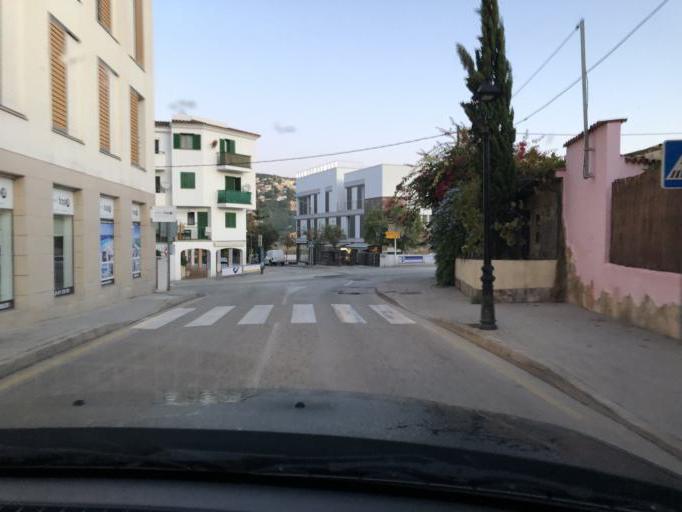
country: ES
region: Balearic Islands
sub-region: Illes Balears
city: Camp de Mar
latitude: 39.5452
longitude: 2.3925
